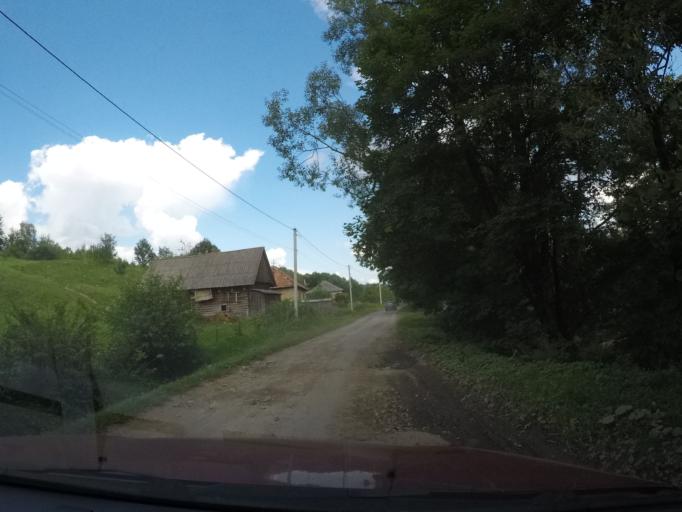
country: UA
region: Zakarpattia
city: Velykyi Bereznyi
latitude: 49.0239
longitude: 22.6089
